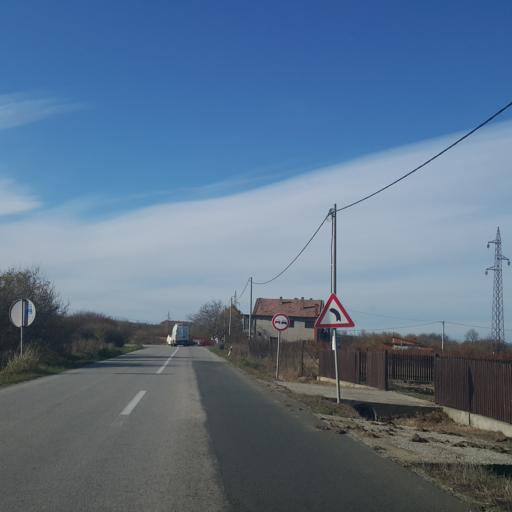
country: RS
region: Central Serbia
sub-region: Sumadijski Okrug
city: Topola
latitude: 44.2528
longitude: 20.7572
